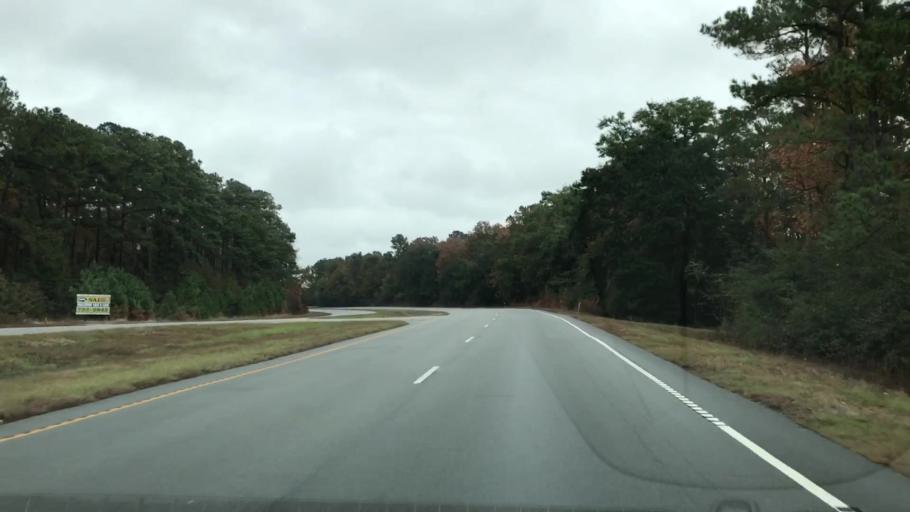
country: US
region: South Carolina
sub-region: Georgetown County
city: Georgetown
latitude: 33.1816
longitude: -79.4091
